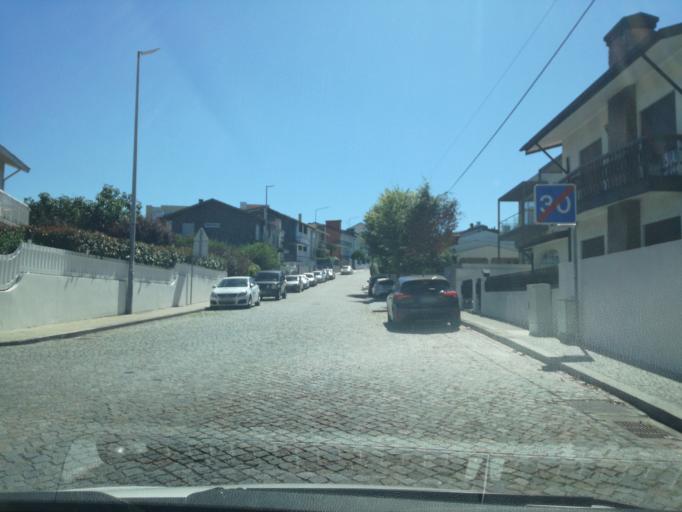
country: PT
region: Porto
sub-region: Maia
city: Maia
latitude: 41.2309
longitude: -8.6171
